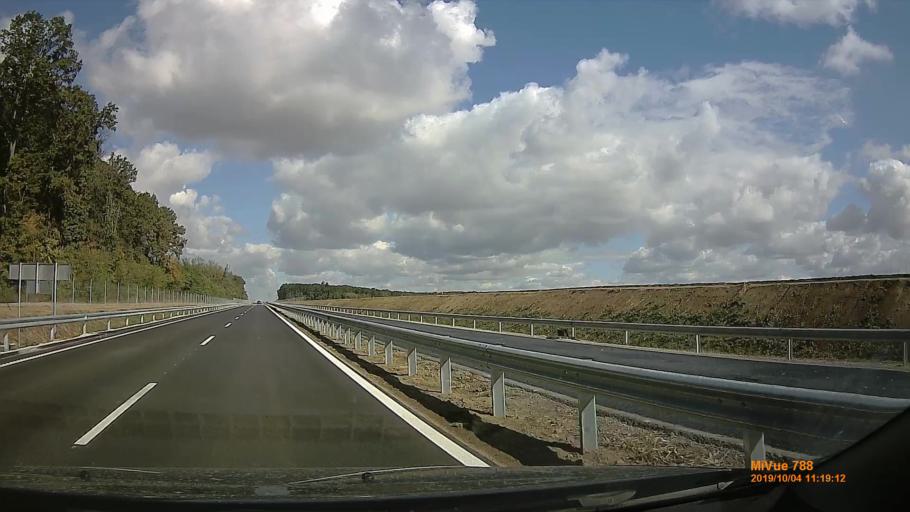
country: HU
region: Somogy
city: Kaposvar
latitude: 46.4795
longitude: 17.8046
